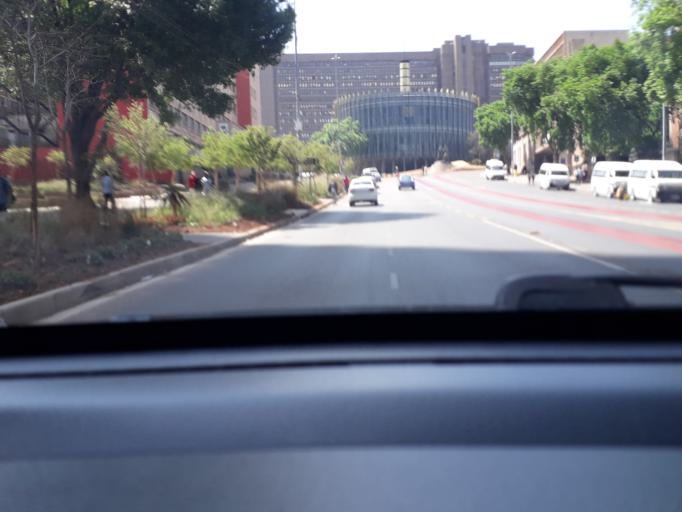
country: ZA
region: Gauteng
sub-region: City of Johannesburg Metropolitan Municipality
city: Johannesburg
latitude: -26.1945
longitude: 28.0406
